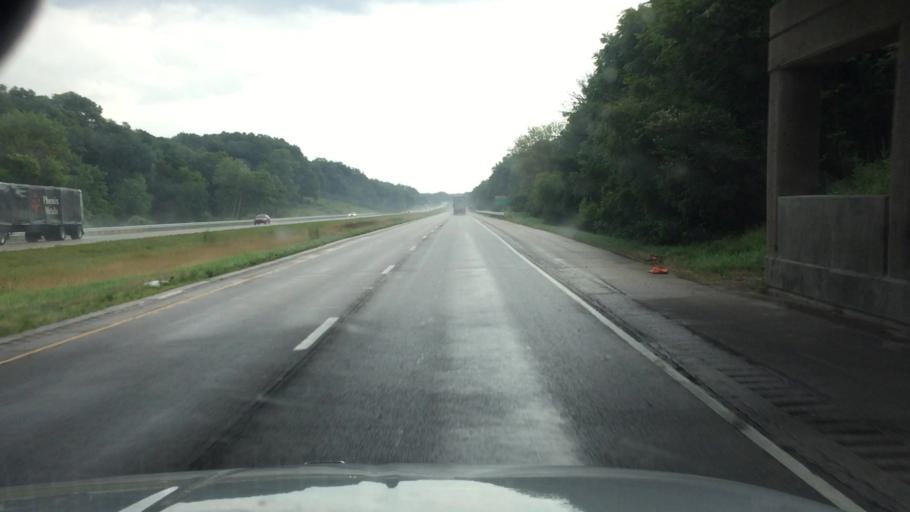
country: US
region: Illinois
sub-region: Peoria County
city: Bellevue
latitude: 40.7563
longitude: -89.7086
